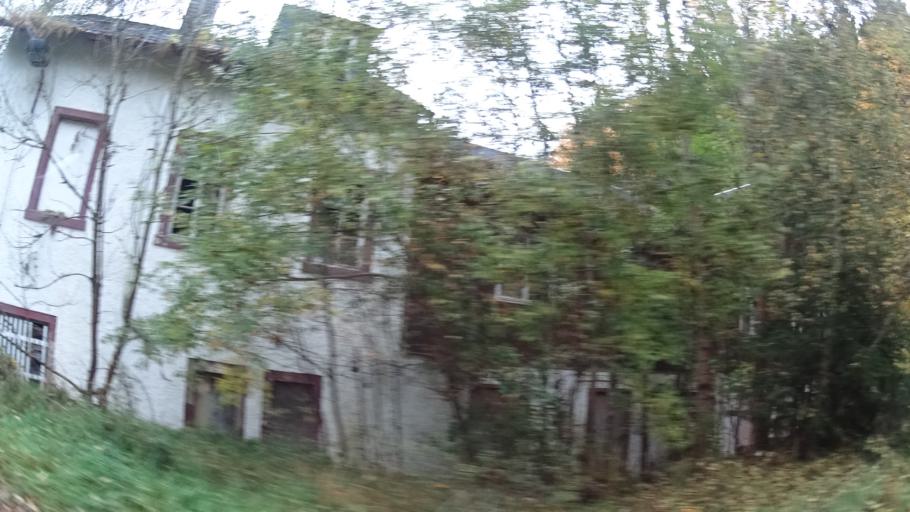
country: DE
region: Thuringia
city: Wurzbach
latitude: 50.4870
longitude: 11.5494
